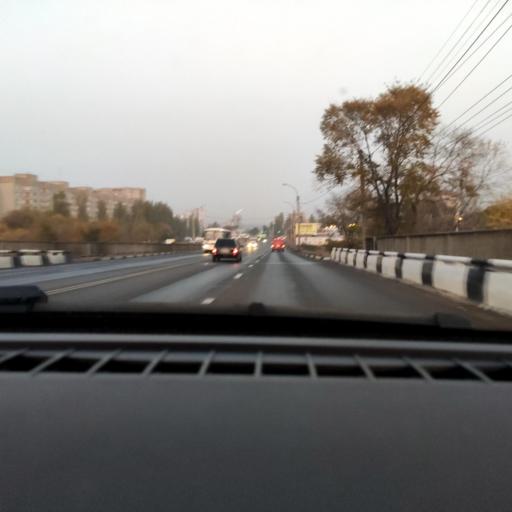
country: RU
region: Voronezj
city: Voronezh
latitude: 51.6843
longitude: 39.2713
